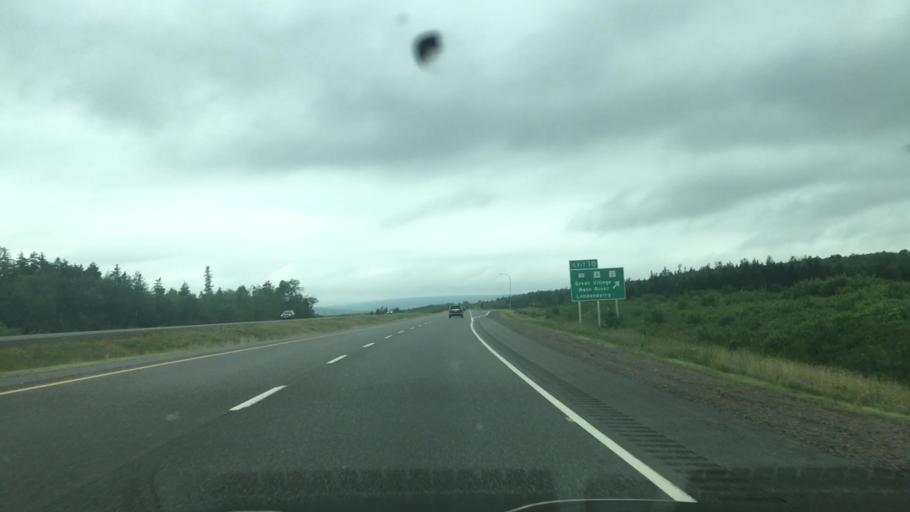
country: CA
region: Nova Scotia
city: Truro
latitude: 45.4339
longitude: -63.5795
